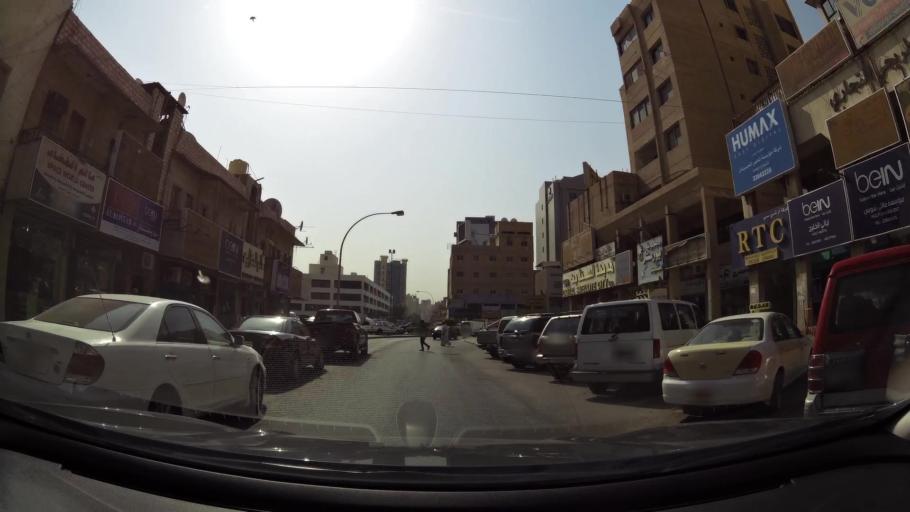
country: KW
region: Muhafazat Hawalli
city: Hawalli
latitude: 29.3364
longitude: 48.0169
